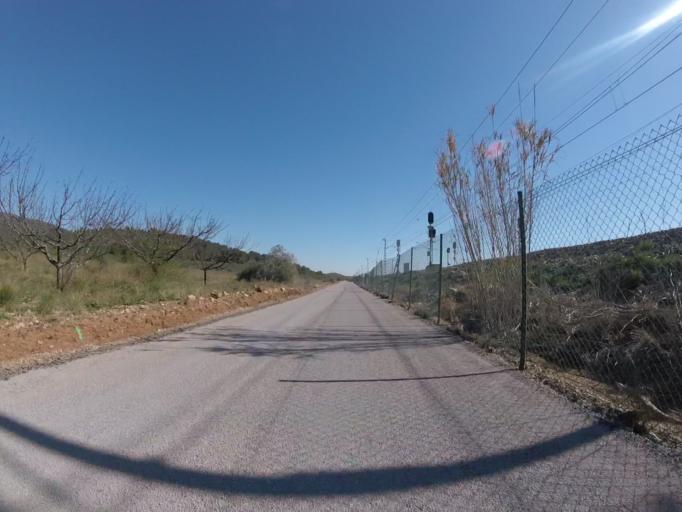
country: ES
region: Valencia
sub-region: Provincia de Castello
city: Santa Magdalena de Pulpis
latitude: 40.3429
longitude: 0.2659
